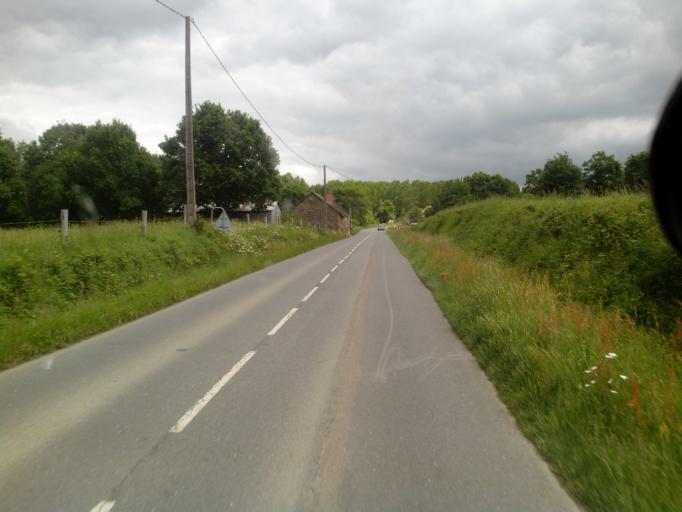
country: FR
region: Brittany
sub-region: Departement d'Ille-et-Vilaine
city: Chasne-sur-Illet
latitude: 48.2468
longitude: -1.5738
